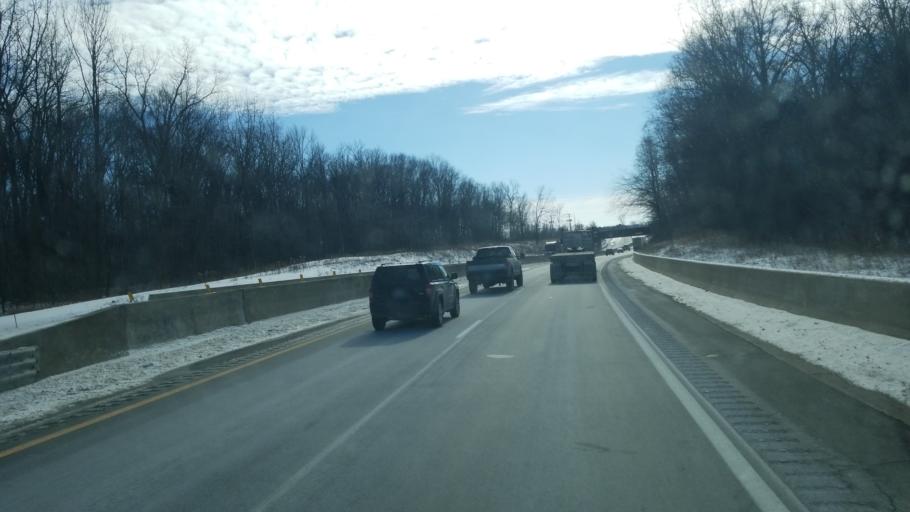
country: US
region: Michigan
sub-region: Washtenaw County
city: Milan
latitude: 42.0413
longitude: -83.6707
